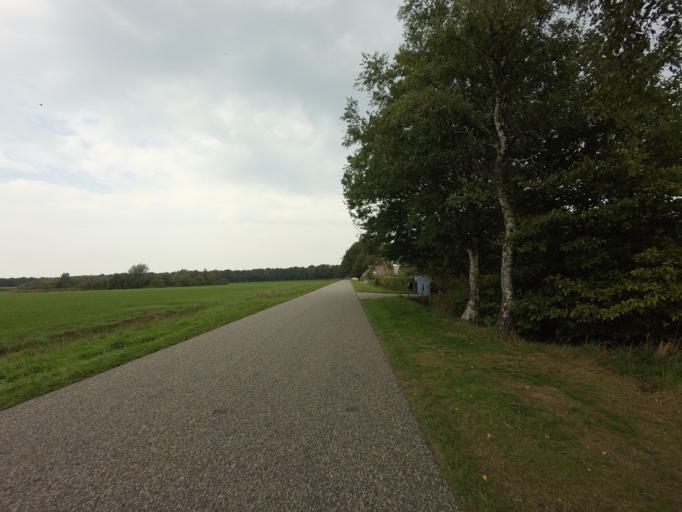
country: NL
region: Drenthe
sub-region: Gemeente Tynaarlo
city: Vries
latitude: 53.0561
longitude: 6.5882
